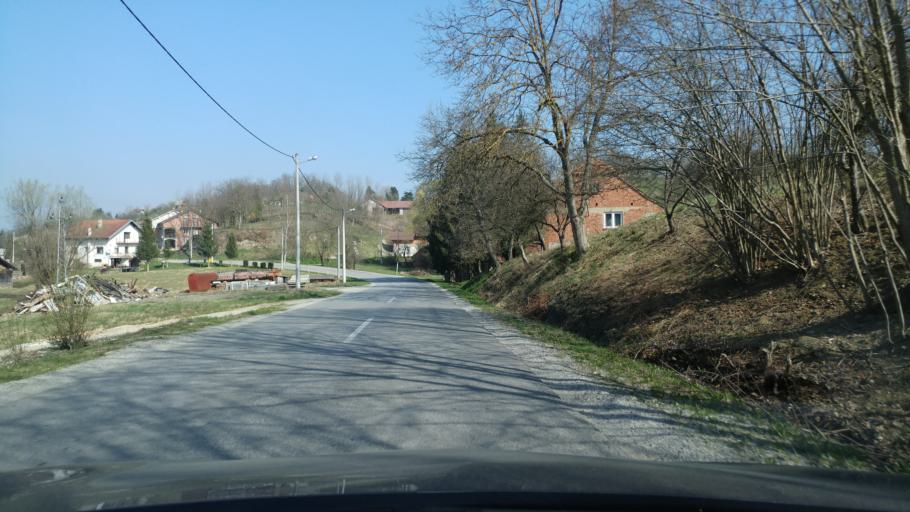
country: HR
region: Zagrebacka
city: Pojatno
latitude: 45.9393
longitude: 15.7586
